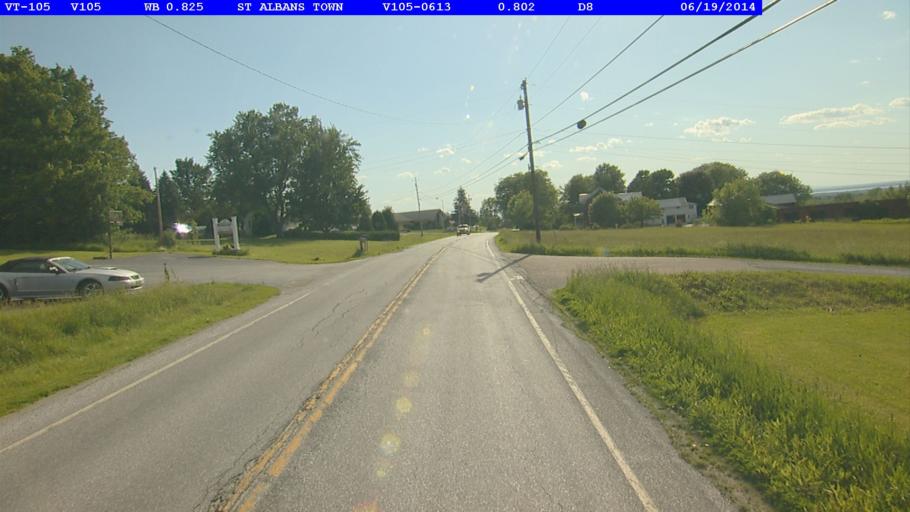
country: US
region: Vermont
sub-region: Franklin County
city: Saint Albans
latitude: 44.8273
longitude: -73.0666
